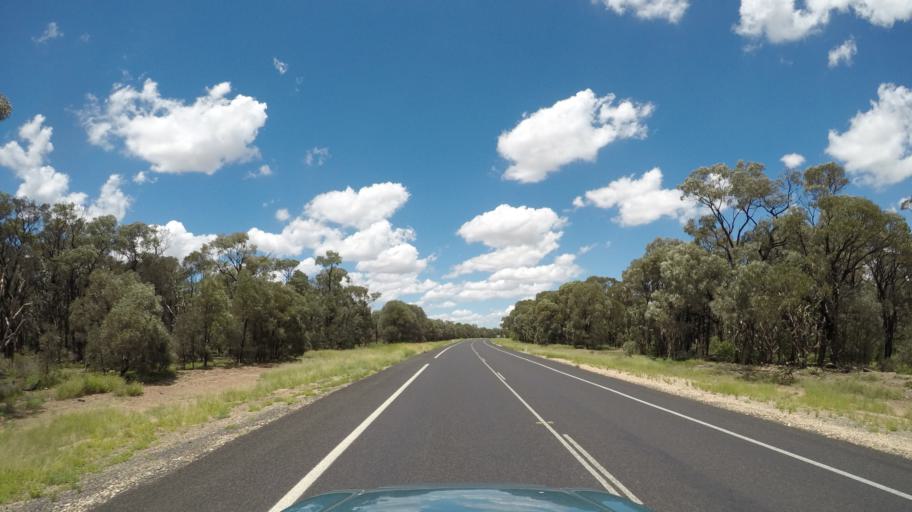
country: AU
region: Queensland
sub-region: Goondiwindi
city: Goondiwindi
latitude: -28.1055
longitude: 150.7219
